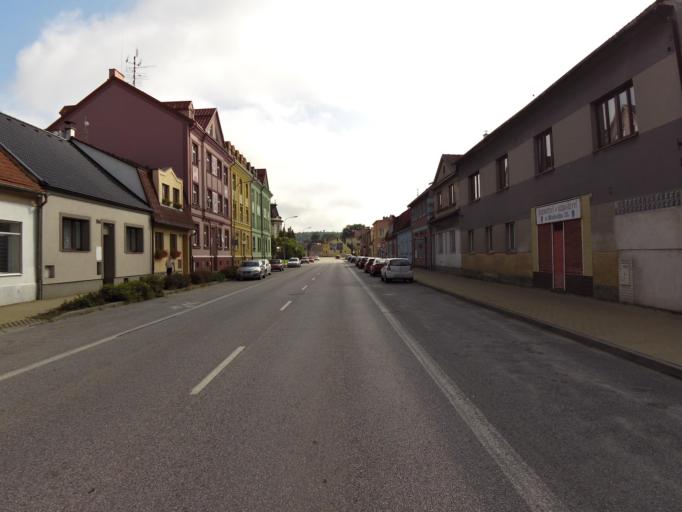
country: CZ
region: Jihocesky
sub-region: Okres Tabor
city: Veseli nad Luznici
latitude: 49.1873
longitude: 14.7089
